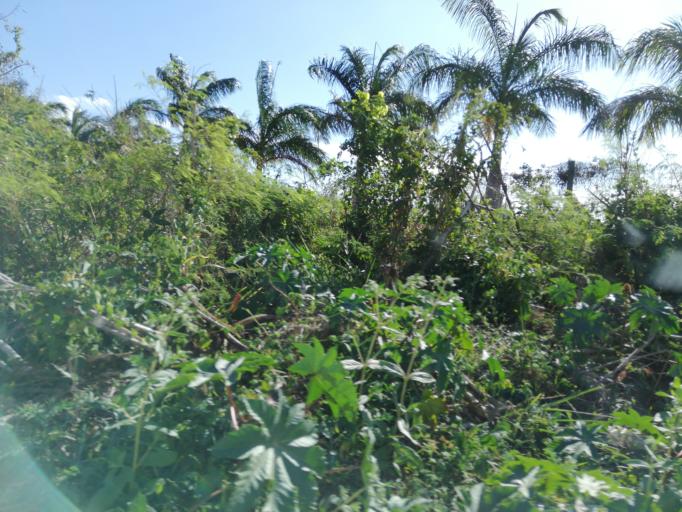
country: MU
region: Riviere du Rempart
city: Petit Raffray
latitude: -20.0158
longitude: 57.6002
